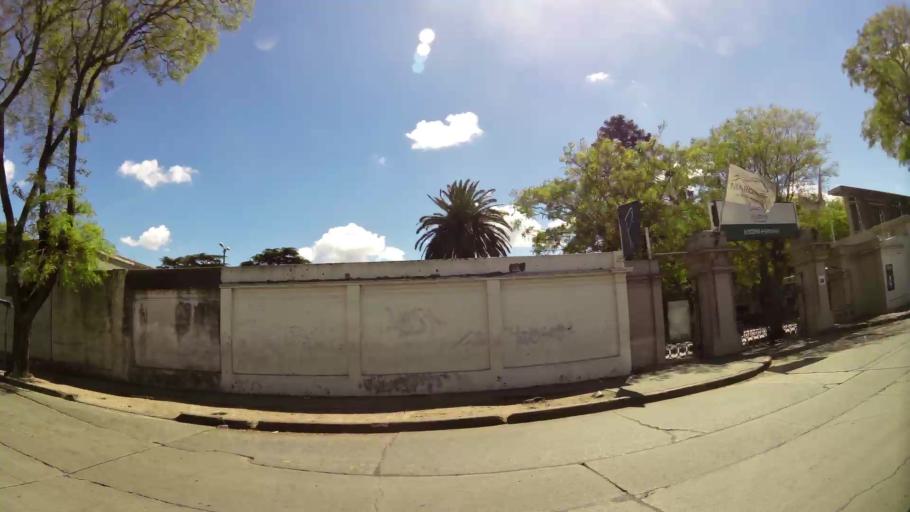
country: UY
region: Montevideo
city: Montevideo
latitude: -34.8409
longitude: -56.1450
